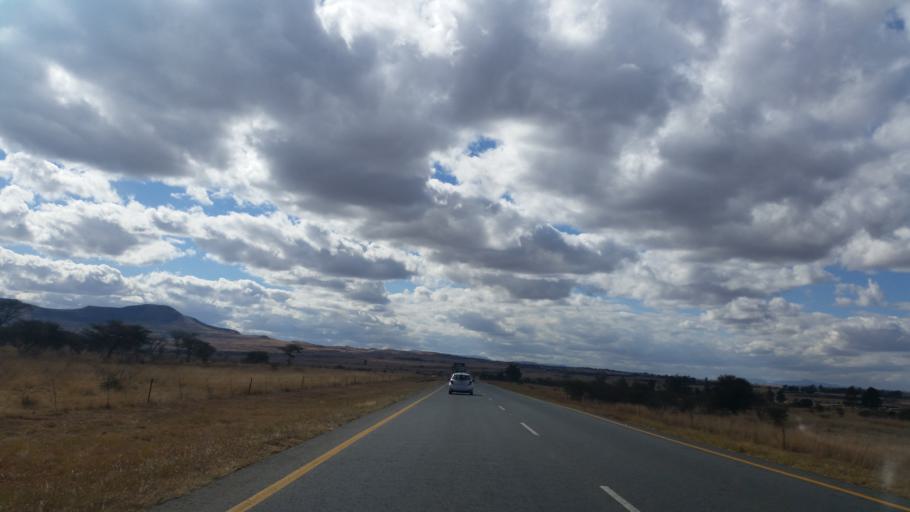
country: ZA
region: KwaZulu-Natal
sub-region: uThukela District Municipality
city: Ladysmith
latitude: -28.4544
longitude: 29.8744
